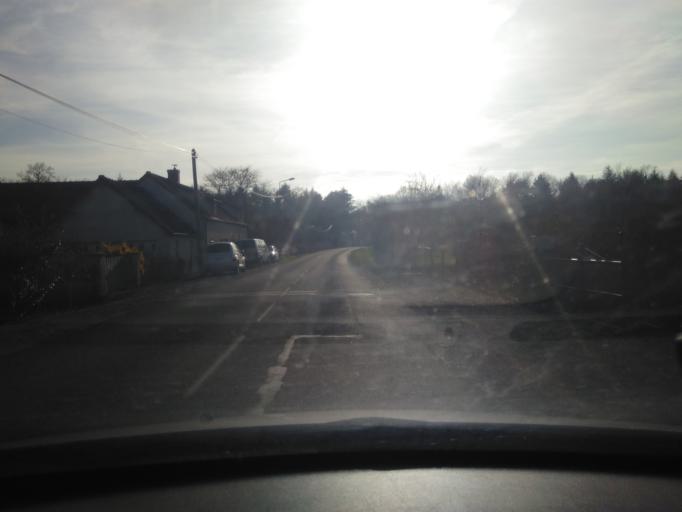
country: FR
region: Bourgogne
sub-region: Departement de la Nievre
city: Saint-Parize-le-Chatel
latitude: 46.8198
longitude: 3.2465
